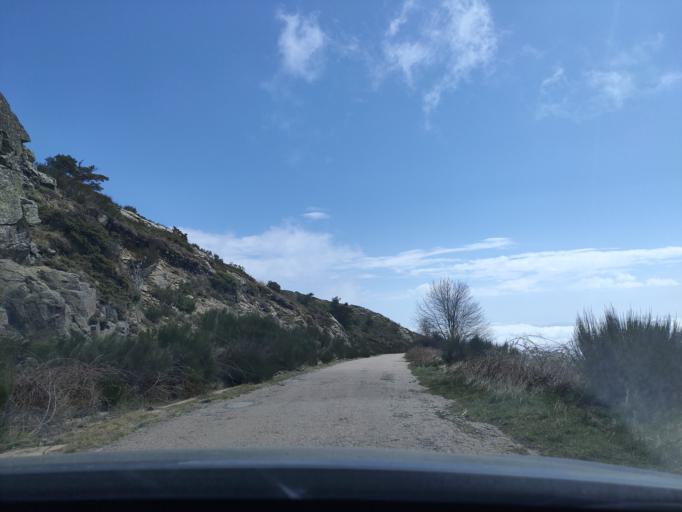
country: ES
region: Catalonia
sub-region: Provincia de Barcelona
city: Fogars de Montclus
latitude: 41.7706
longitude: 2.4434
